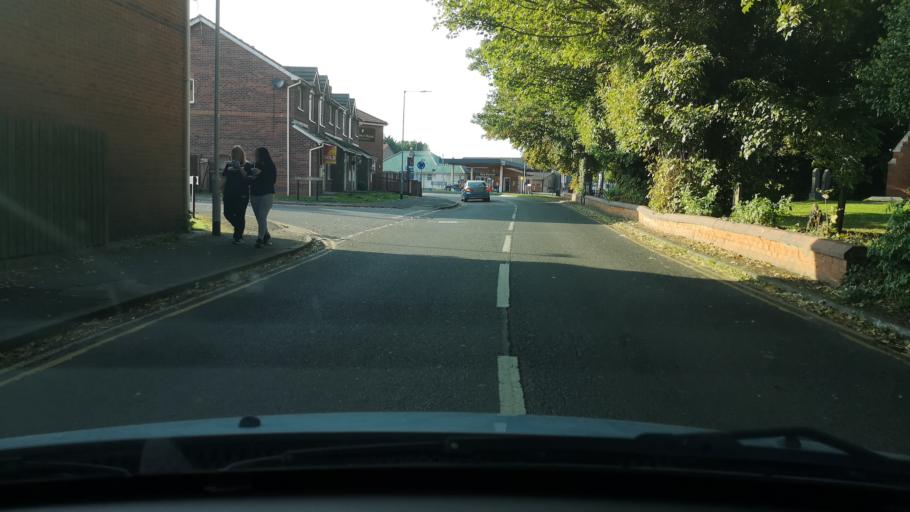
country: GB
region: England
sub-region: East Riding of Yorkshire
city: Skelton
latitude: 53.6902
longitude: -0.8319
